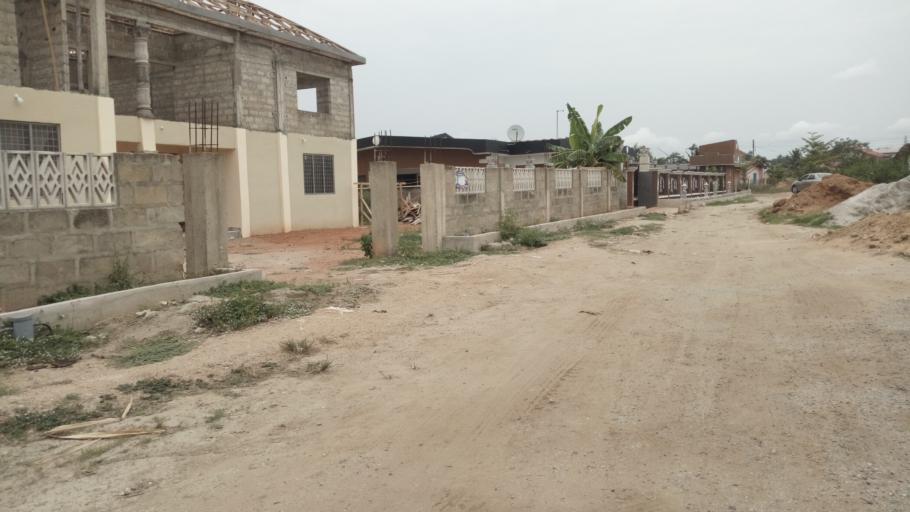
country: GH
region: Central
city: Winneba
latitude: 5.3639
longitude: -0.6393
